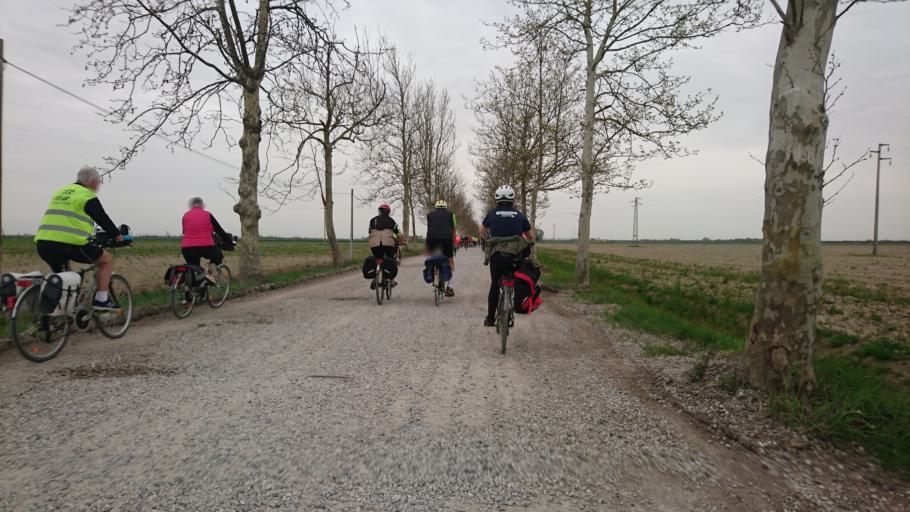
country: IT
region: Veneto
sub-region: Provincia di Venezia
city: Lugugnana
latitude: 45.6757
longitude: 12.9680
